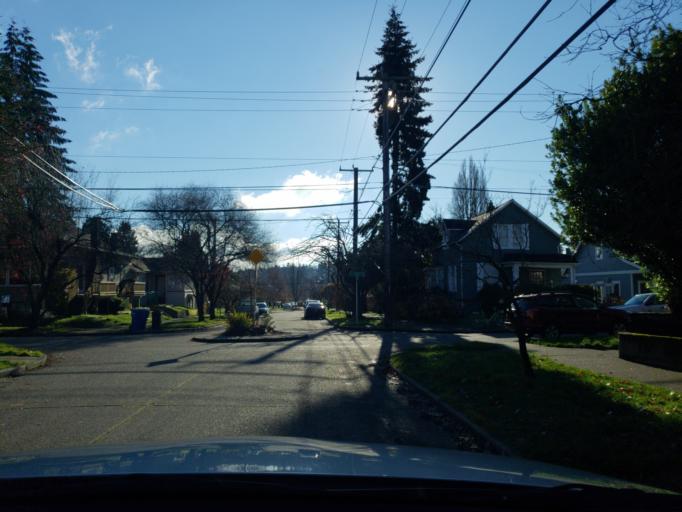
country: US
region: Washington
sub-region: King County
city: Shoreline
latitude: 47.6820
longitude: -122.3499
